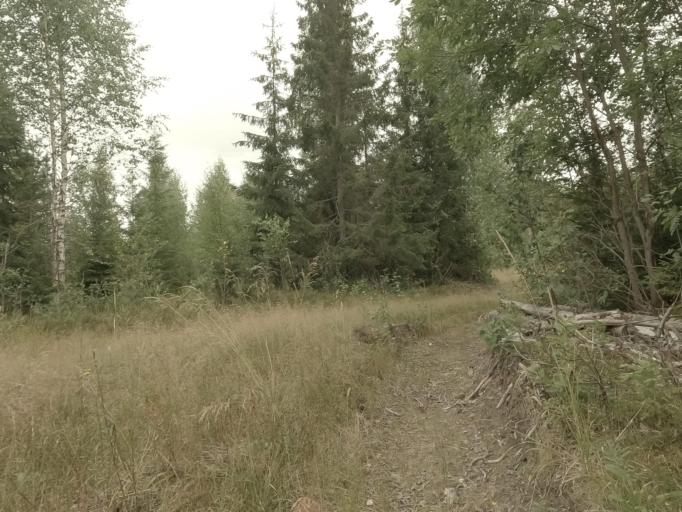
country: RU
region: Leningrad
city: Kamennogorsk
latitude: 61.0467
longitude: 29.1857
